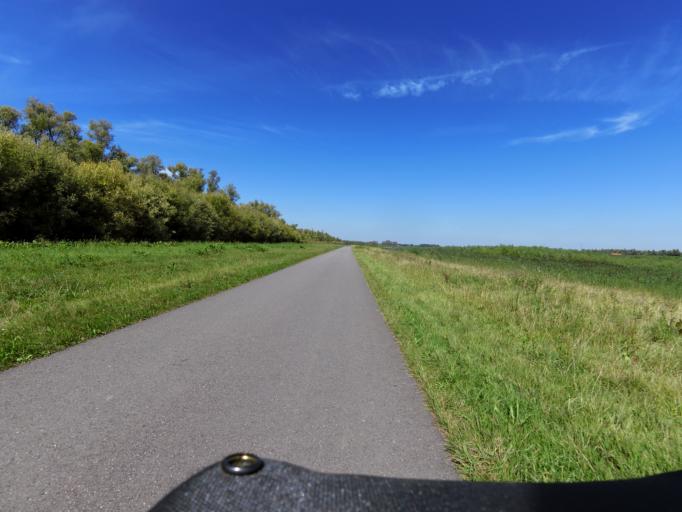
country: NL
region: South Holland
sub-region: Gemeente Sliedrecht
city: Sliedrecht
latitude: 51.7624
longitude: 4.7550
